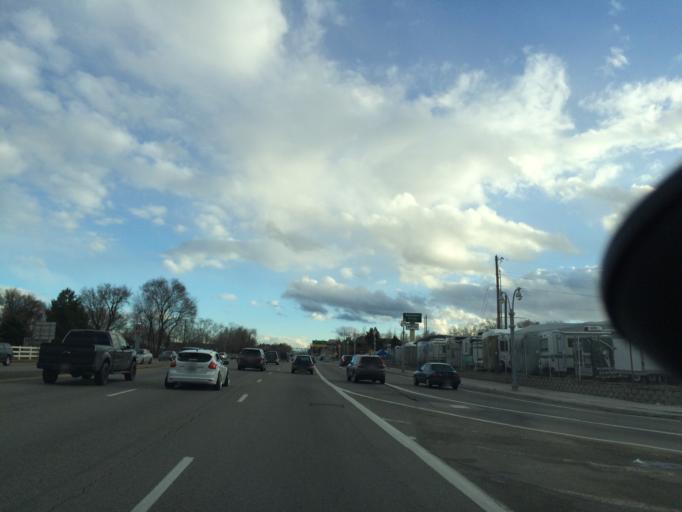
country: US
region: Utah
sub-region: Salt Lake County
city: Taylorsville
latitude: 40.6428
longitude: -111.9389
